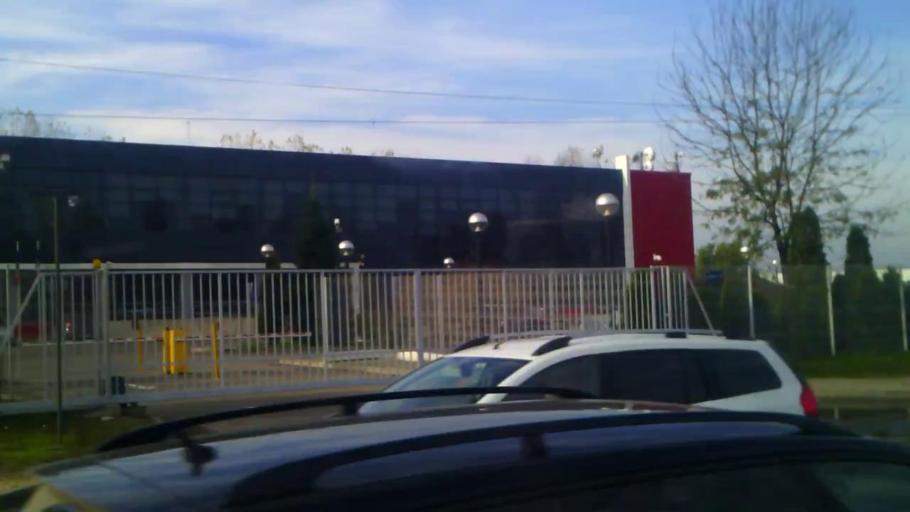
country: RO
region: Ilfov
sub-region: Comuna Berceni
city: Berceni
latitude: 44.3429
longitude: 26.1631
